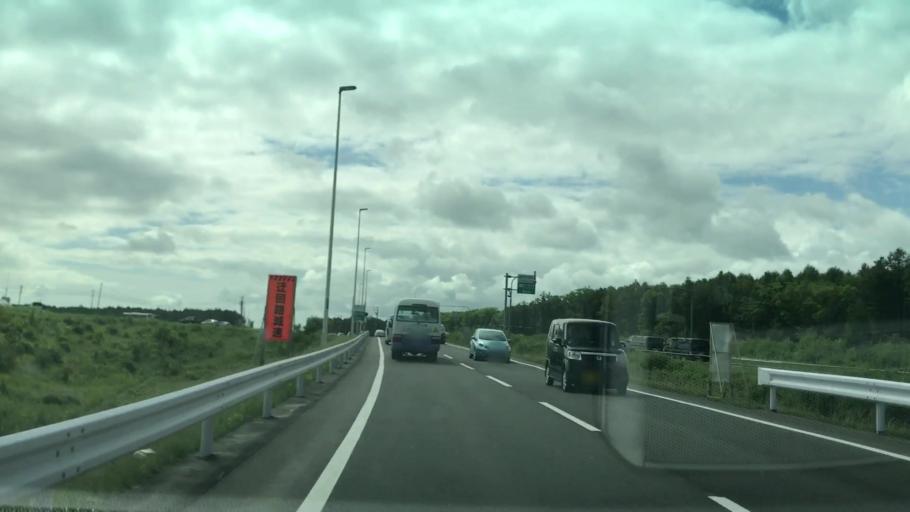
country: JP
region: Hokkaido
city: Chitose
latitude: 42.7740
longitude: 141.6790
